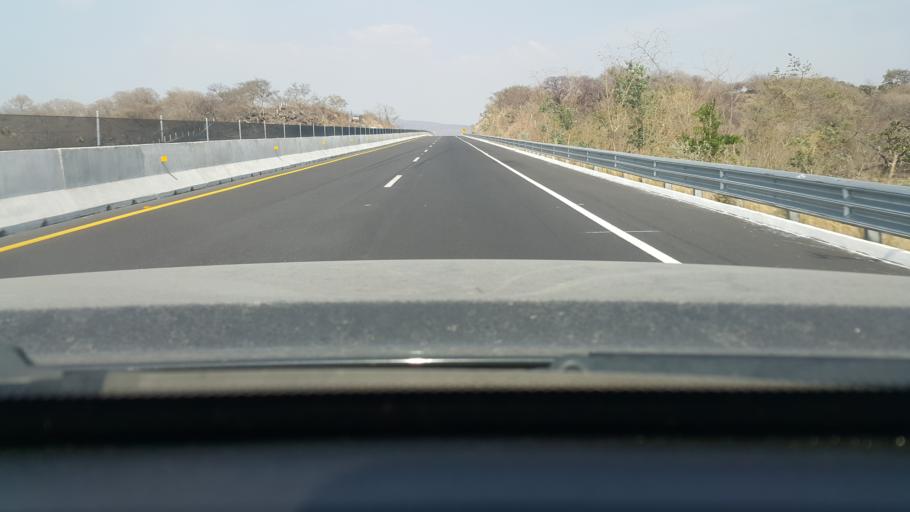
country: MX
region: Nayarit
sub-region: Ahuacatlan
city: Ahuacatlan
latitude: 21.0669
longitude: -104.4713
